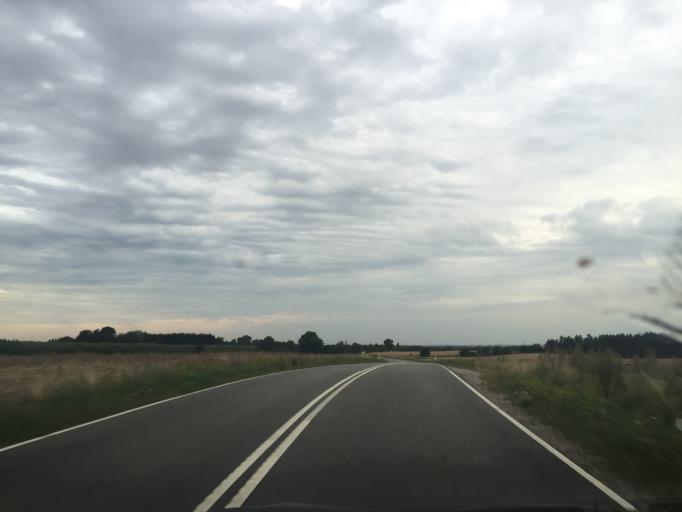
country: DK
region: Capital Region
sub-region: Egedal Kommune
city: Vekso
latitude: 55.7181
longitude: 12.2087
